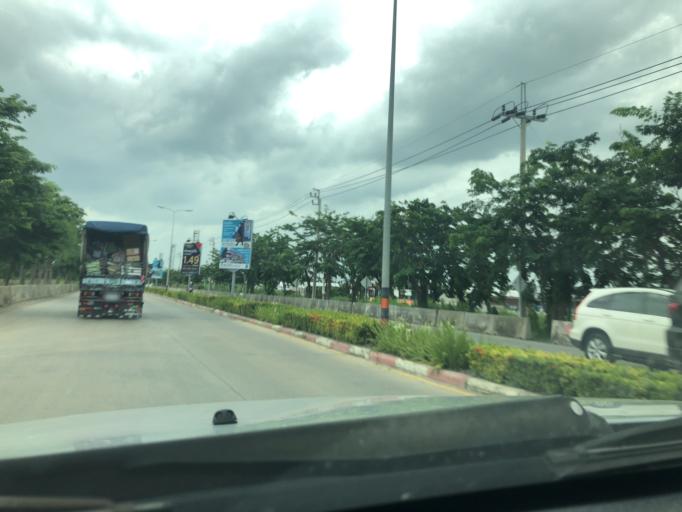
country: TH
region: Nonthaburi
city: Pak Kret
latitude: 13.9250
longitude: 100.5438
